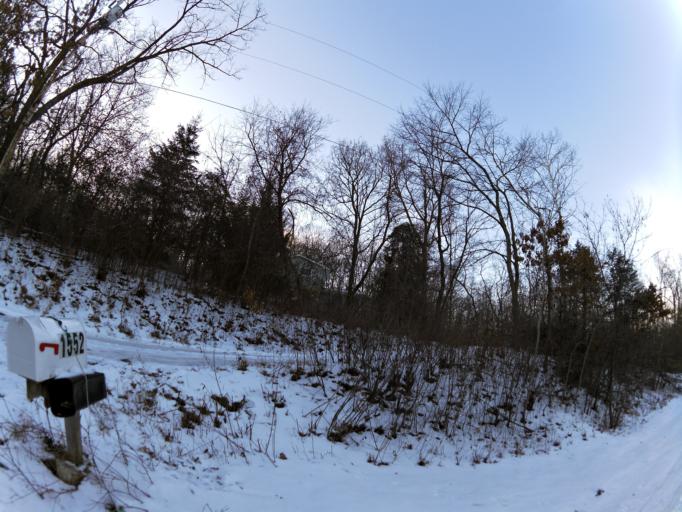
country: US
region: Minnesota
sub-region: Washington County
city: Lake Elmo
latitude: 44.9718
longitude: -92.8377
